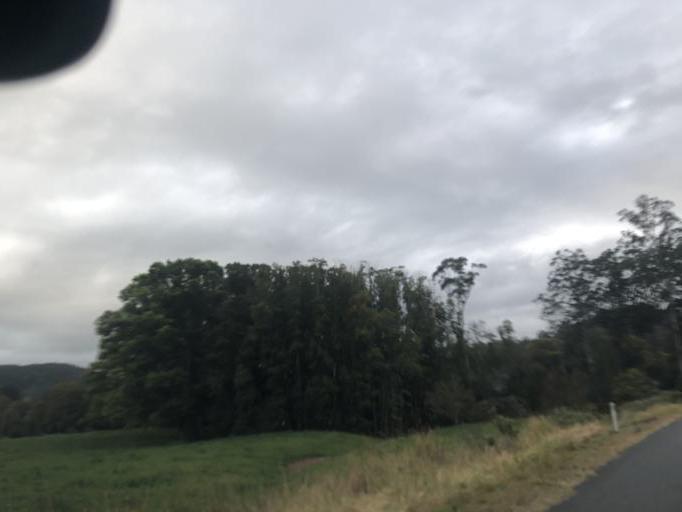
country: AU
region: New South Wales
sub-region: Coffs Harbour
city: Boambee
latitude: -30.2624
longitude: 153.0145
